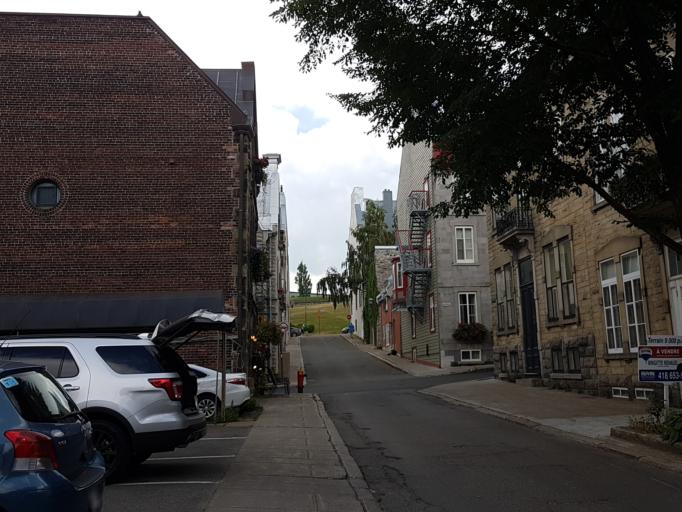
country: CA
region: Quebec
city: Quebec
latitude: 46.8105
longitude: -71.2066
